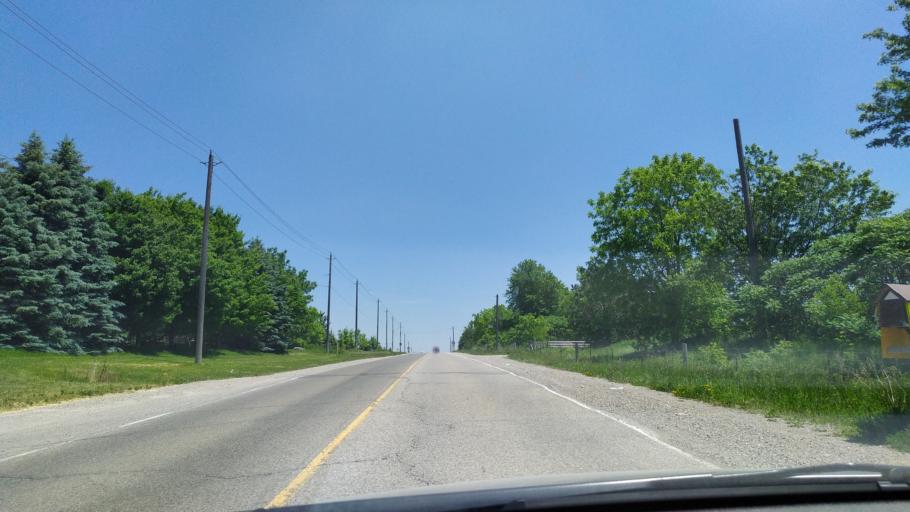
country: CA
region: Ontario
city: Kitchener
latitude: 43.3981
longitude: -80.5276
